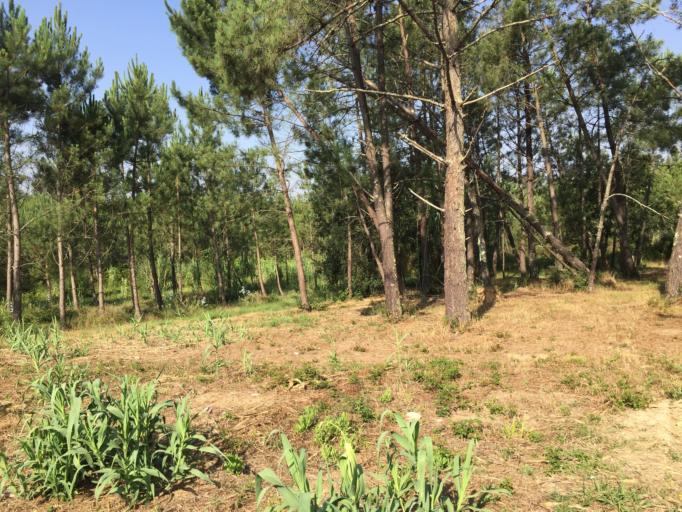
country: PT
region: Coimbra
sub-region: Cantanhede
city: Cantanhede
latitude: 40.4213
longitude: -8.5428
